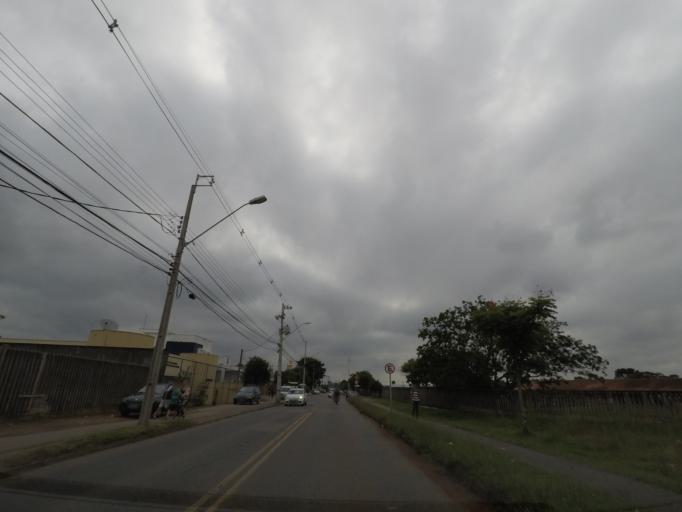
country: BR
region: Parana
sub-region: Curitiba
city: Curitiba
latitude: -25.4965
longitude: -49.3352
